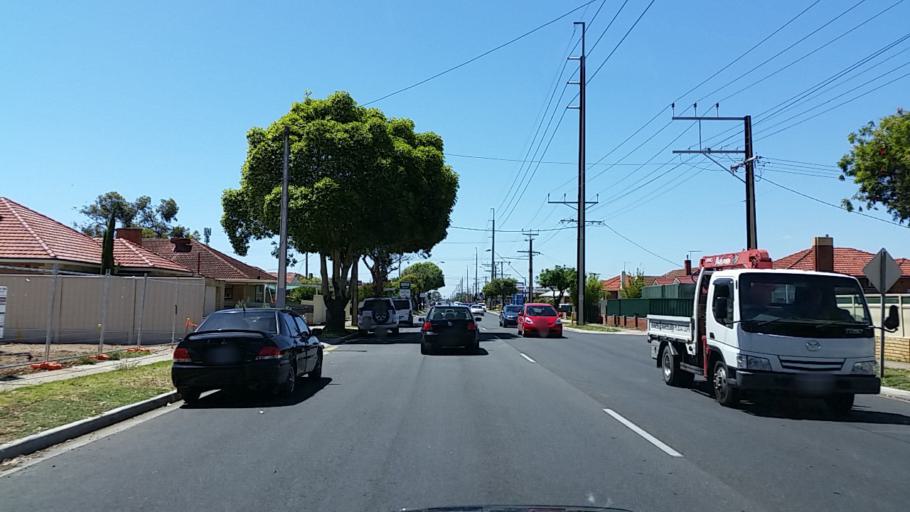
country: AU
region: South Australia
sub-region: Charles Sturt
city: Findon
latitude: -34.8971
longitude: 138.5320
